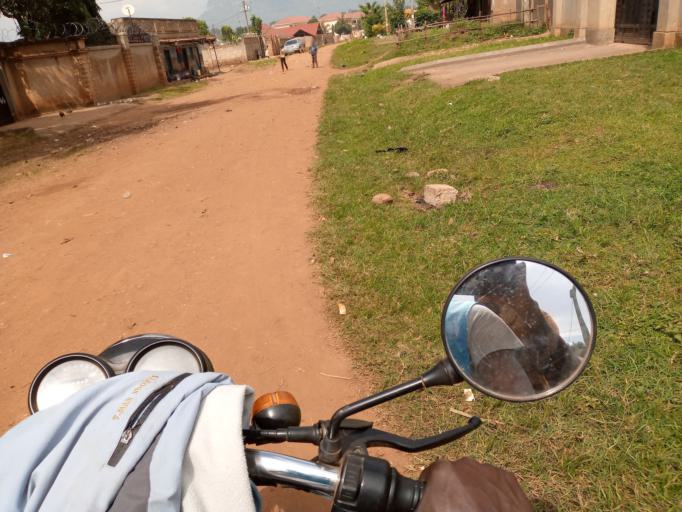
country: UG
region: Eastern Region
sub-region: Mbale District
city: Mbale
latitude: 1.0837
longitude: 34.1583
